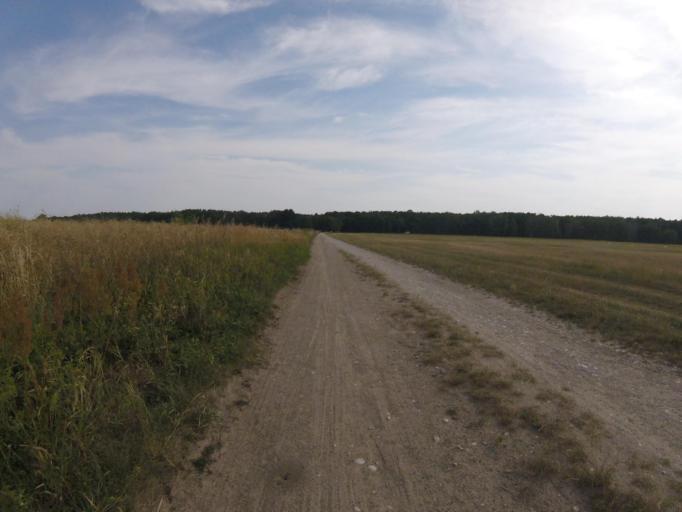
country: DE
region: Brandenburg
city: Spreenhagen
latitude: 52.2810
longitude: 13.8108
